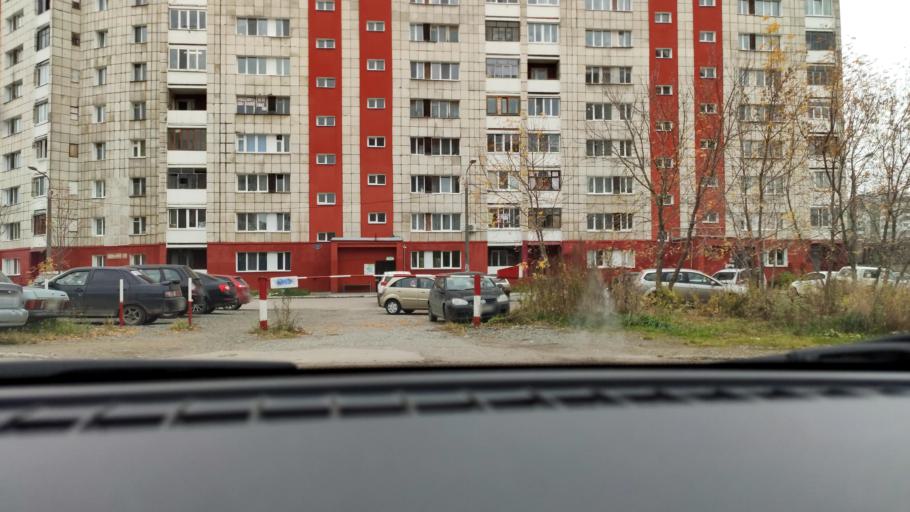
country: RU
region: Perm
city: Perm
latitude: 58.0583
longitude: 56.3469
